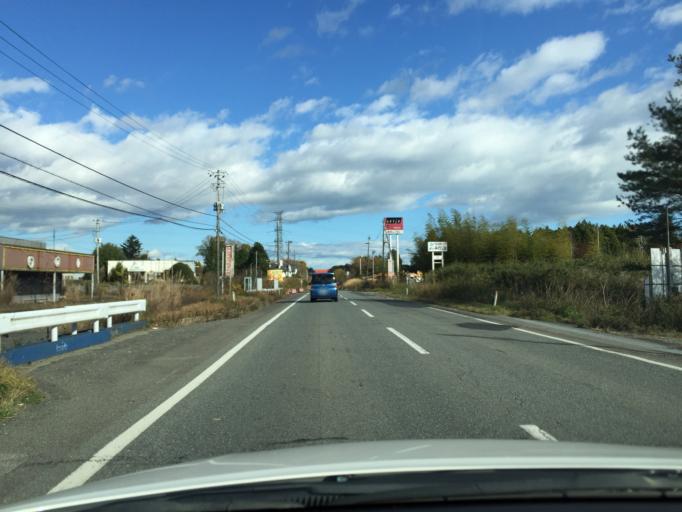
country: JP
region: Fukushima
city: Namie
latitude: 37.4213
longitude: 141.0026
